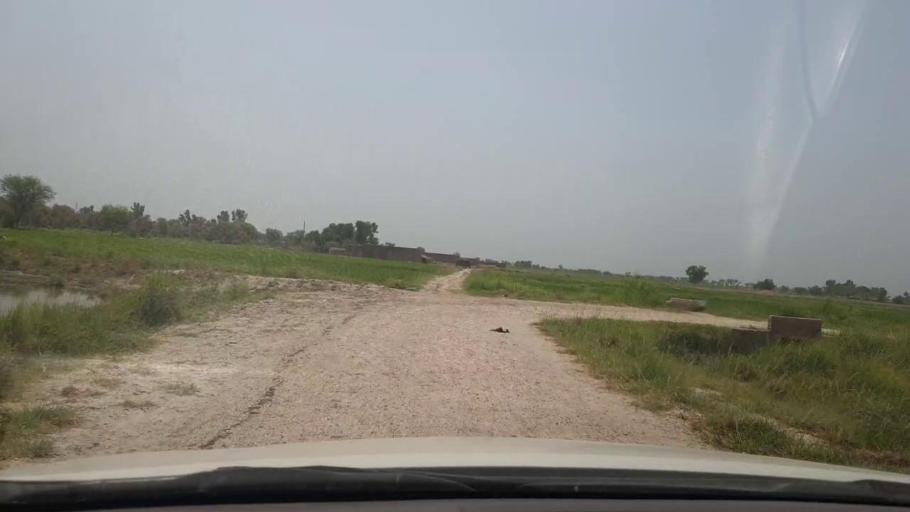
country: PK
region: Sindh
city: Shikarpur
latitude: 28.0243
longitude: 68.6125
